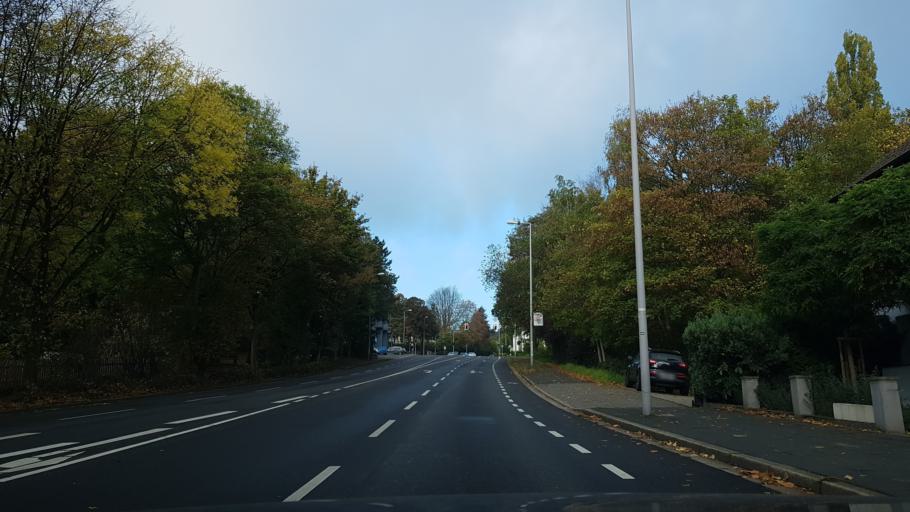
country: DE
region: North Rhine-Westphalia
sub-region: Regierungsbezirk Dusseldorf
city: Muelheim (Ruhr)
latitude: 51.4088
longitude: 6.8667
